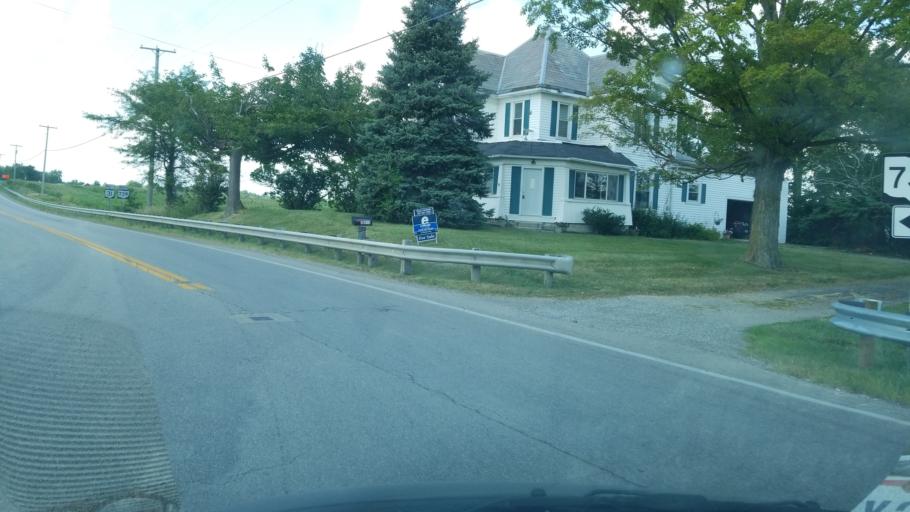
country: US
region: Ohio
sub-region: Union County
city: Richwood
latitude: 40.4461
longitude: -83.4492
